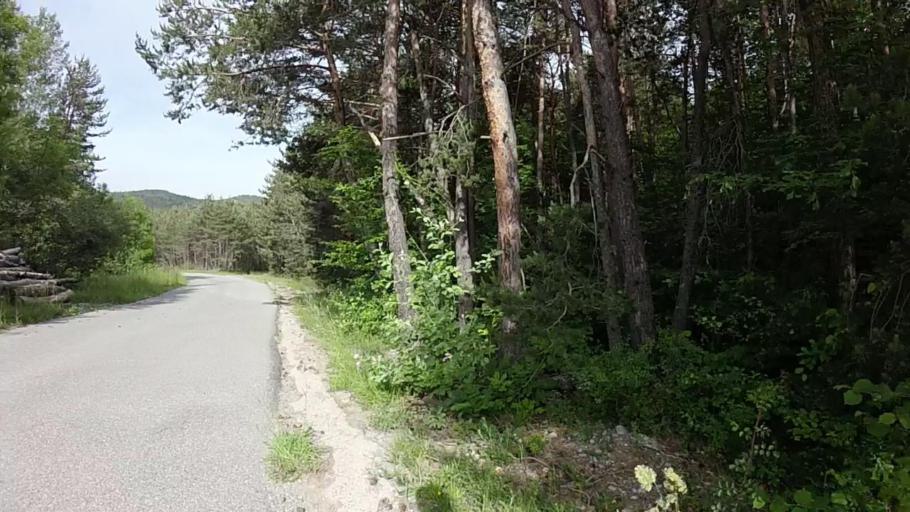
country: FR
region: Provence-Alpes-Cote d'Azur
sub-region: Departement des Alpes-de-Haute-Provence
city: Seyne-les-Alpes
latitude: 44.4095
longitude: 6.3447
